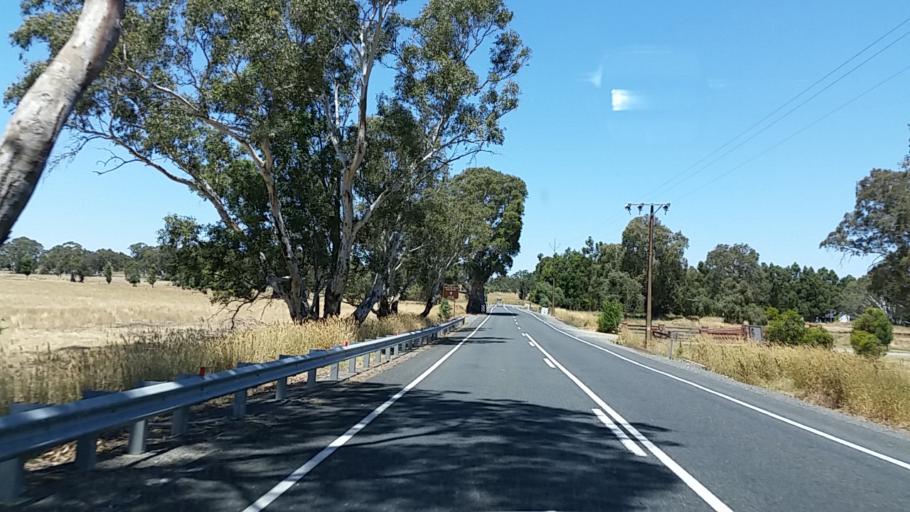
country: AU
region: South Australia
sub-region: Adelaide Hills
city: Birdwood
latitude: -34.7962
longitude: 139.0067
